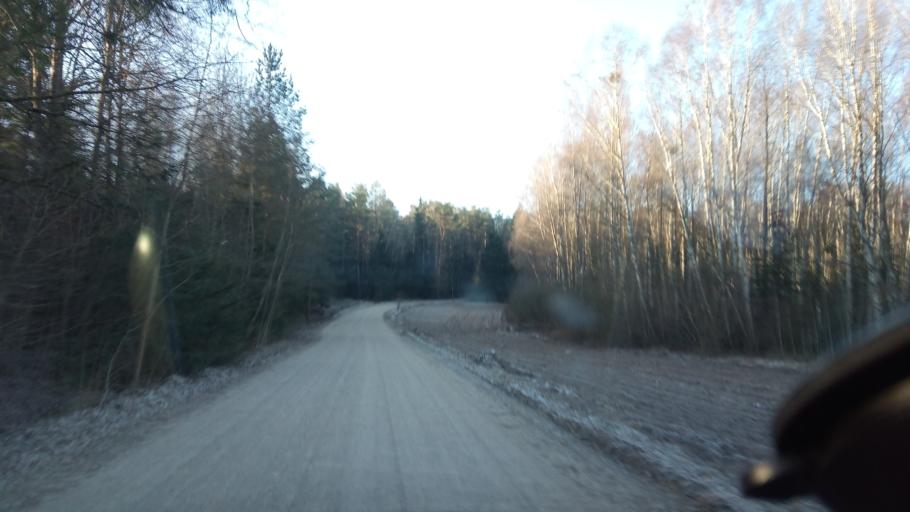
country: LT
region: Alytaus apskritis
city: Druskininkai
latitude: 54.1570
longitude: 23.9512
